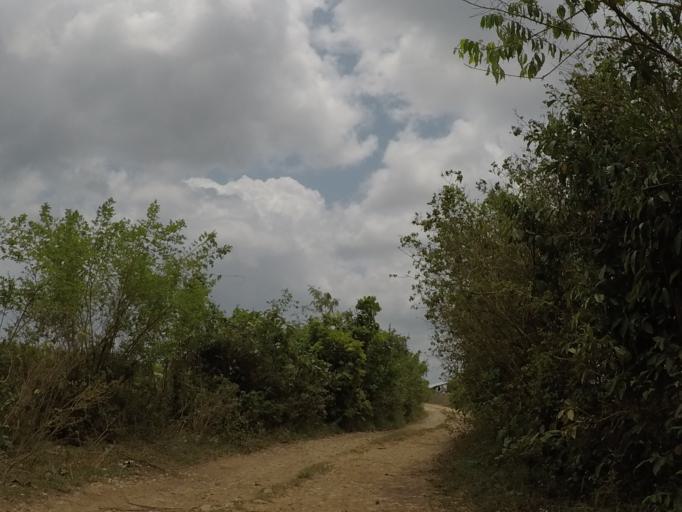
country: TZ
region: Zanzibar Central/South
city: Koani
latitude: -6.1743
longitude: 39.3110
